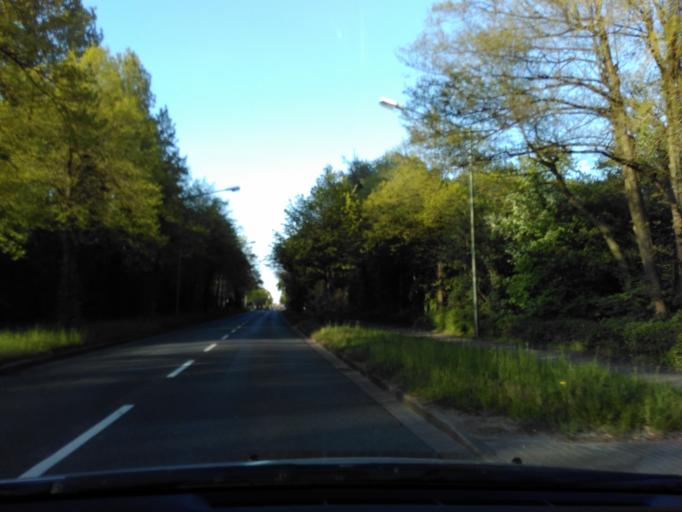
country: DE
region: Lower Saxony
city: Osnabrueck
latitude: 52.2588
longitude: 7.9971
